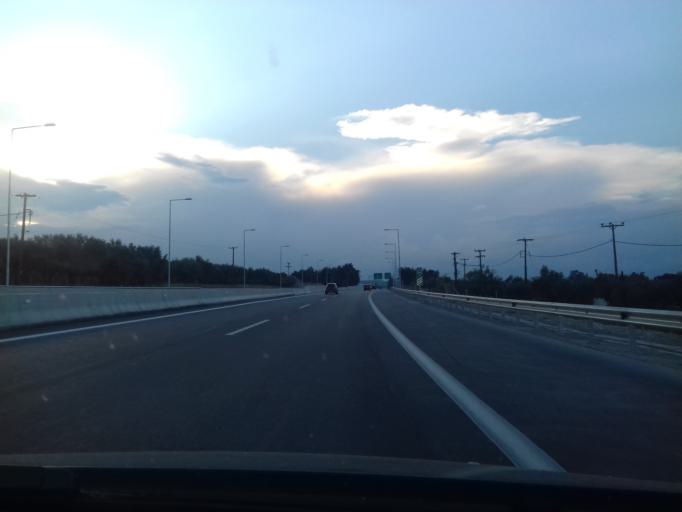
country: GR
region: West Greece
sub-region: Nomos Achaias
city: Temeni
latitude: 38.2175
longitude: 22.1094
